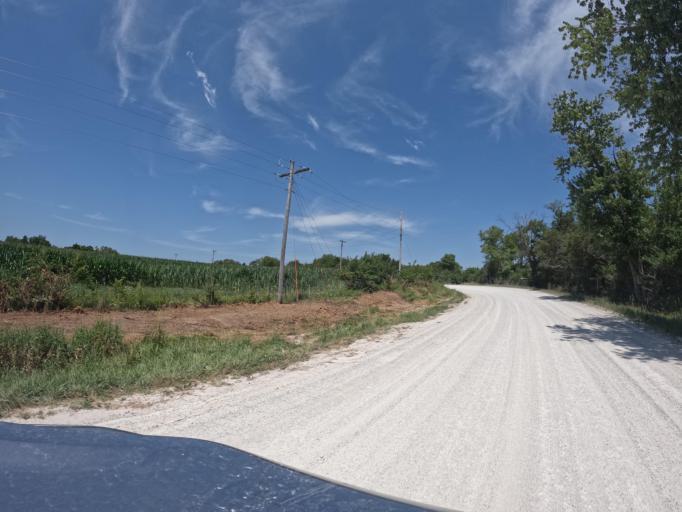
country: US
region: Iowa
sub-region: Henry County
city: Mount Pleasant
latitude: 40.9041
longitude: -91.5363
